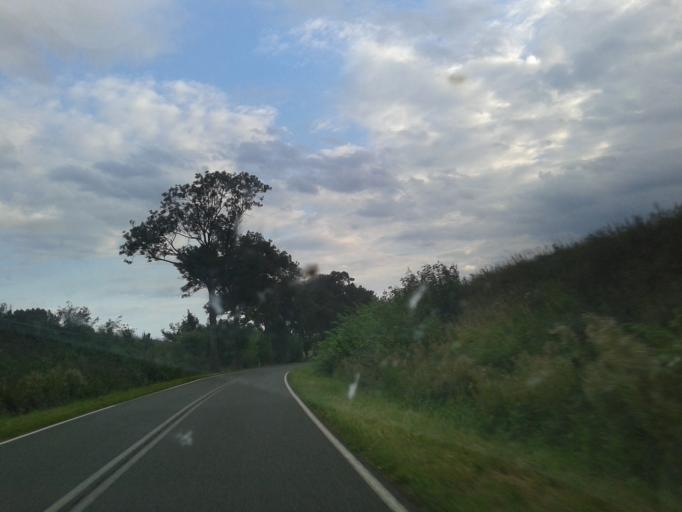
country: PL
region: West Pomeranian Voivodeship
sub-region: Powiat szczecinecki
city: Grzmiaca
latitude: 53.8807
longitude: 16.4990
